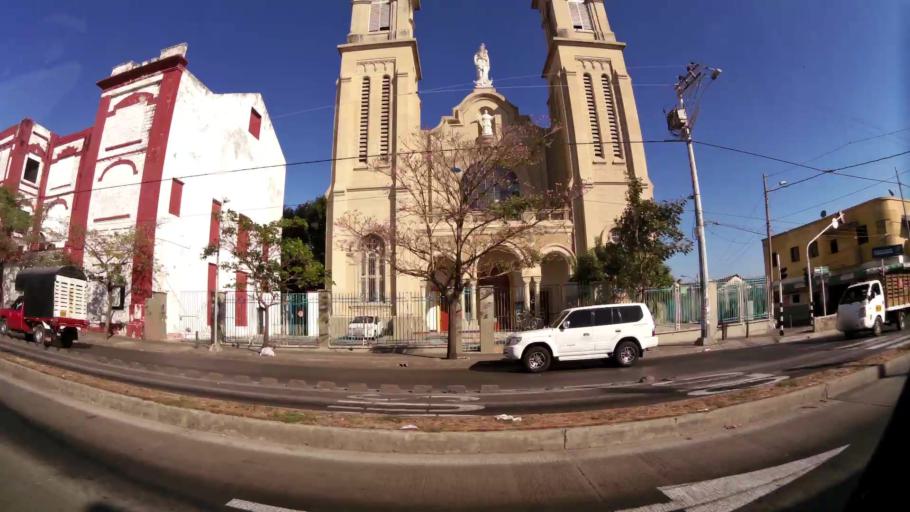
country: CO
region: Atlantico
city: Barranquilla
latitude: 10.9721
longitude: -74.7895
